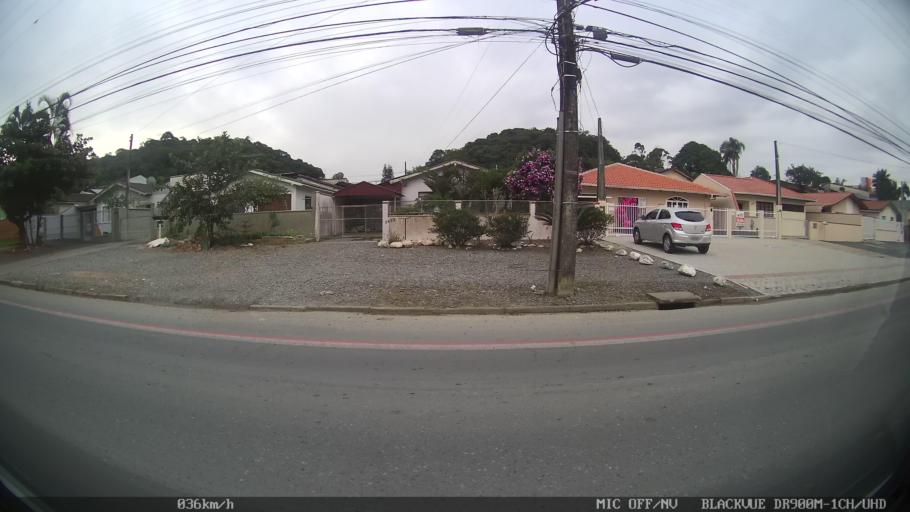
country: BR
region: Santa Catarina
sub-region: Joinville
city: Joinville
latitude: -26.2845
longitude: -48.8817
